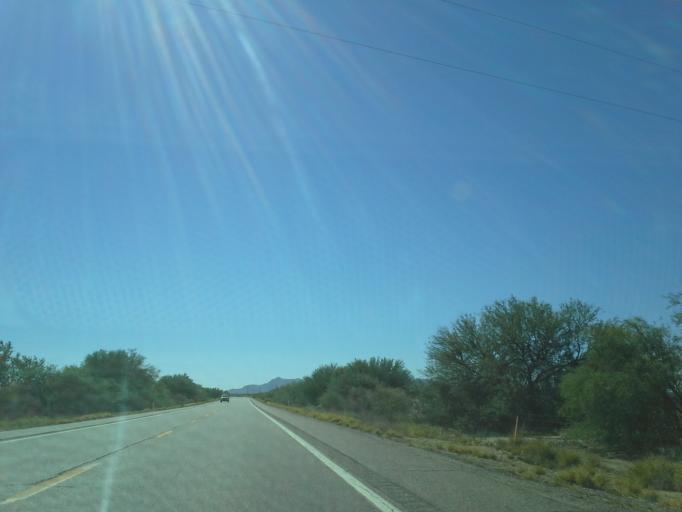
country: US
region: Arizona
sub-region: Pinal County
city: Sacaton
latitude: 33.1304
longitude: -111.7497
